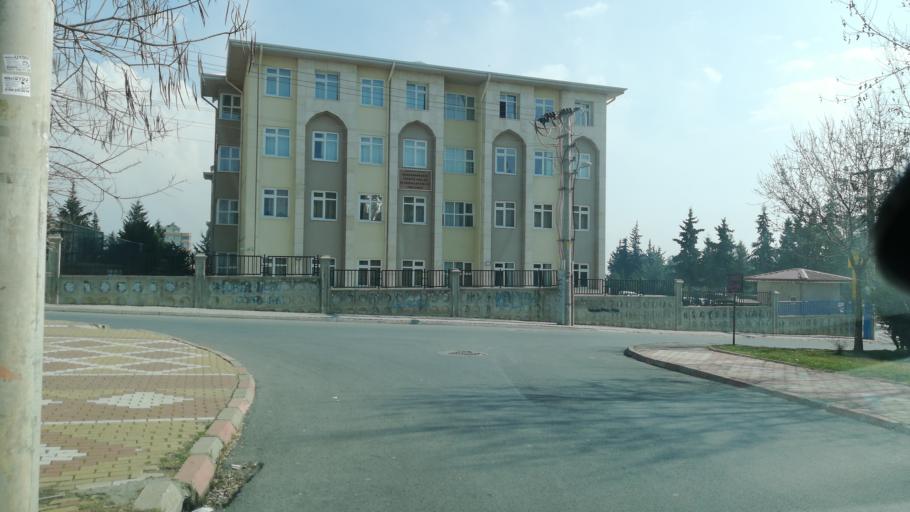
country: TR
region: Kahramanmaras
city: Kahramanmaras
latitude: 37.5880
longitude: 36.9002
